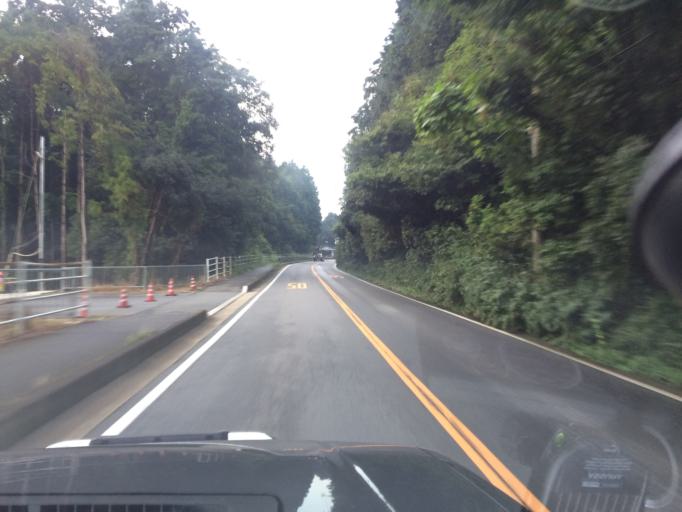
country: JP
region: Hyogo
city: Nishiwaki
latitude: 35.1309
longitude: 135.0124
